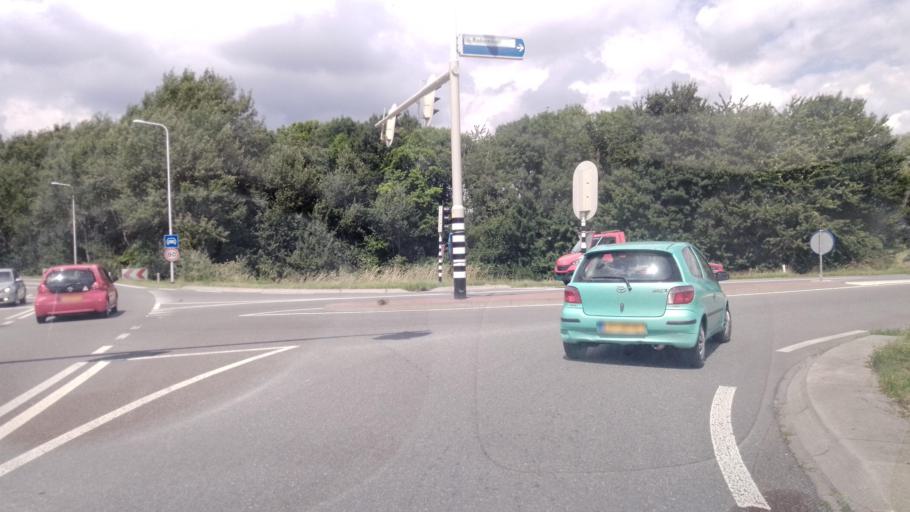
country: NL
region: Gelderland
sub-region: Gemeente Arnhem
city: Arnhem
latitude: 51.9573
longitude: 5.9303
